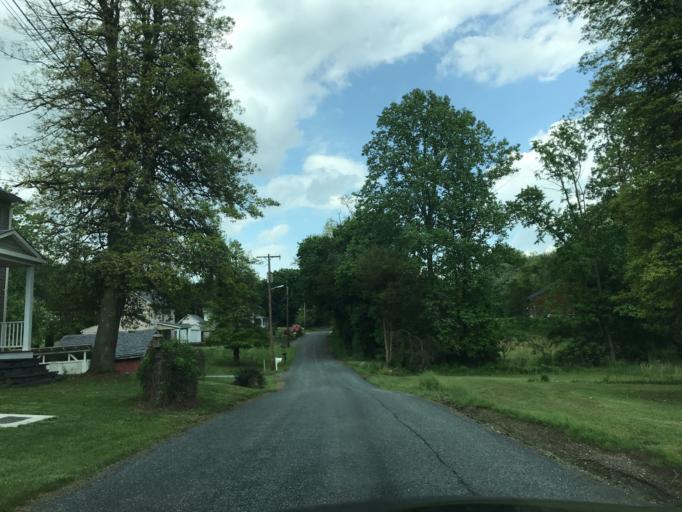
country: US
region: Pennsylvania
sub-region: York County
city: Susquehanna Trails
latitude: 39.7175
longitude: -76.3162
